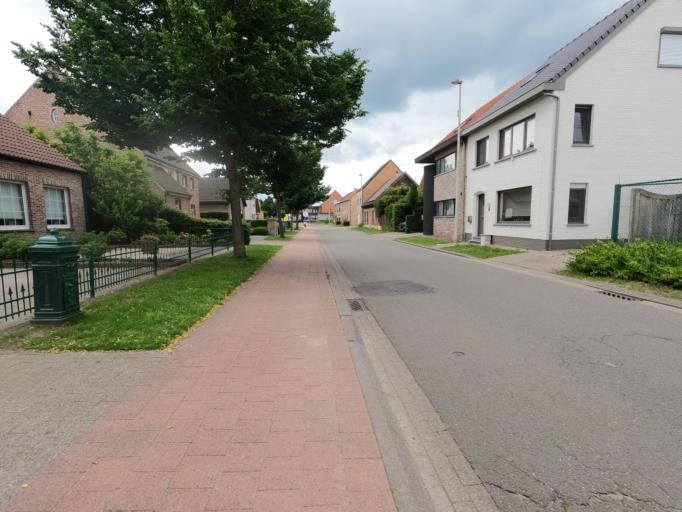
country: BE
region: Flanders
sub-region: Provincie Antwerpen
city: Essen
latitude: 51.4310
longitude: 4.5108
